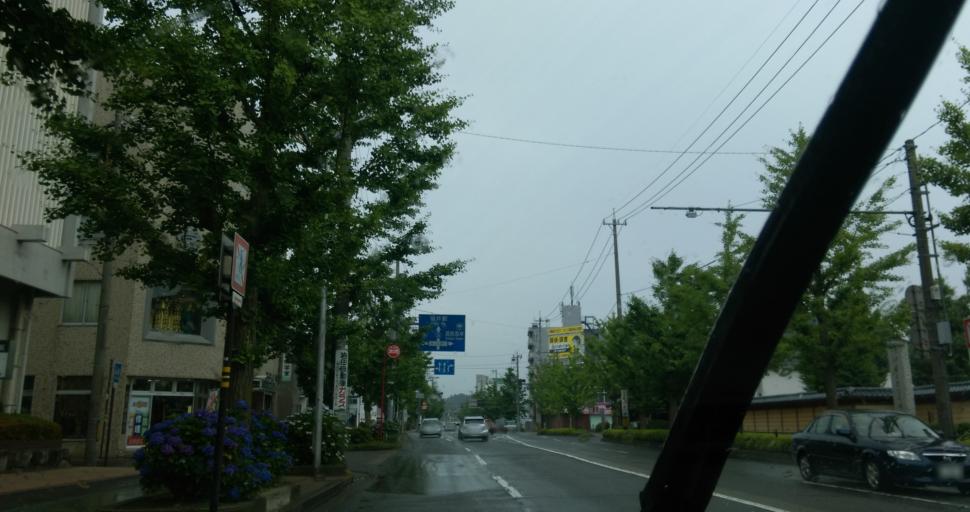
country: JP
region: Fukui
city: Fukui-shi
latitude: 36.0687
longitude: 136.2125
